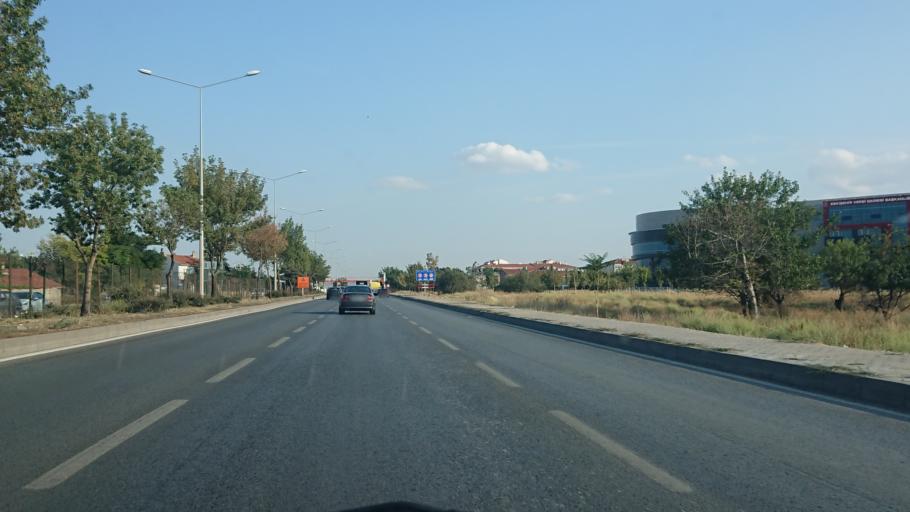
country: TR
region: Eskisehir
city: Eskisehir
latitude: 39.7697
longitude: 30.5613
